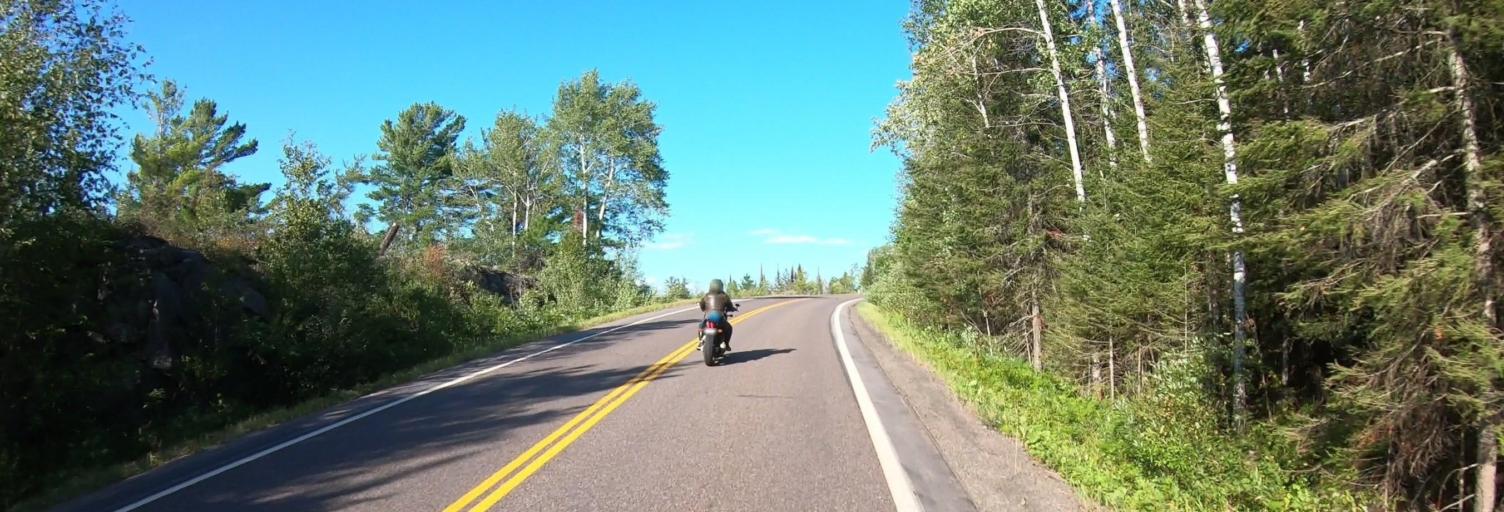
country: US
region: Minnesota
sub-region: Saint Louis County
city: Ely
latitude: 47.9593
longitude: -91.5911
